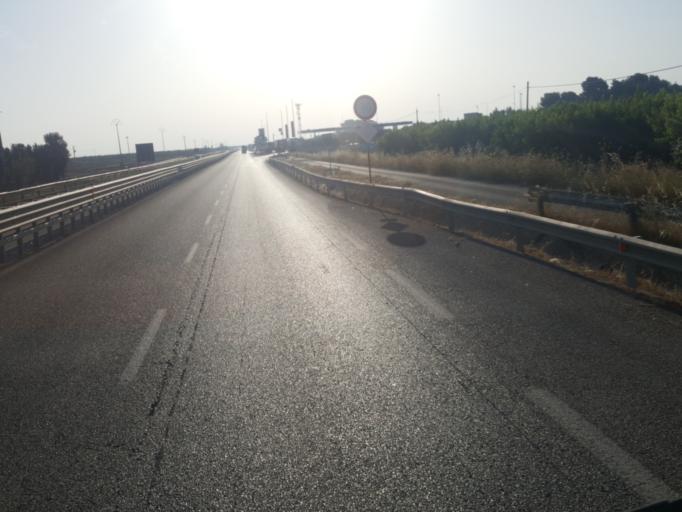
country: IT
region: Apulia
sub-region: Provincia di Foggia
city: Cerignola
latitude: 41.2660
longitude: 15.9390
